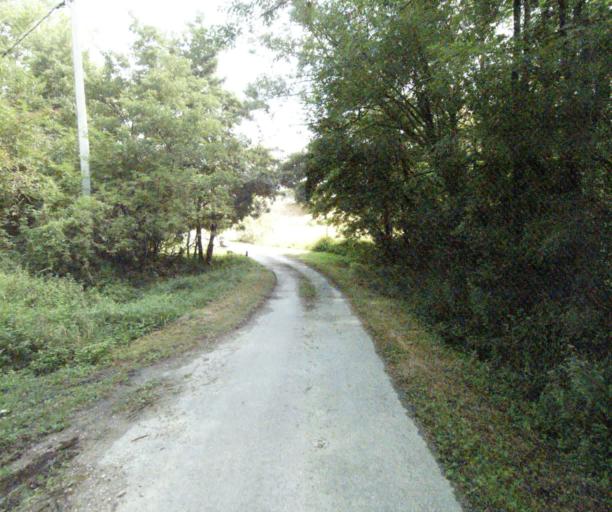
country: FR
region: Midi-Pyrenees
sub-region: Departement du Tarn
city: Dourgne
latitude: 43.4711
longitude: 2.1157
